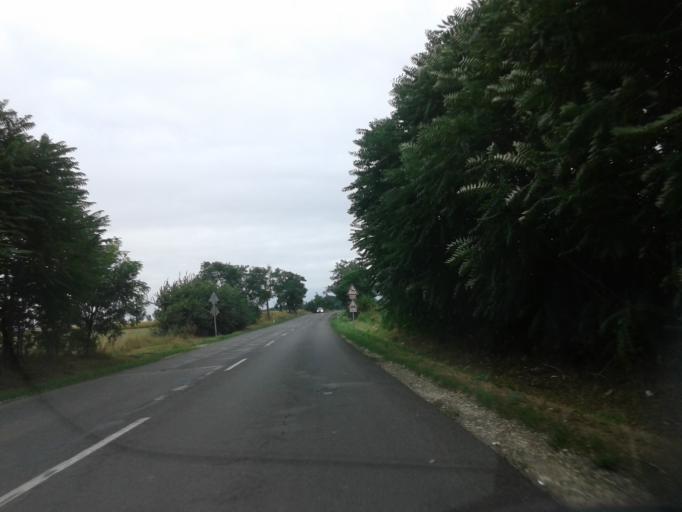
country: HU
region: Pest
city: Kiskunlachaza
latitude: 47.2258
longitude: 19.0209
